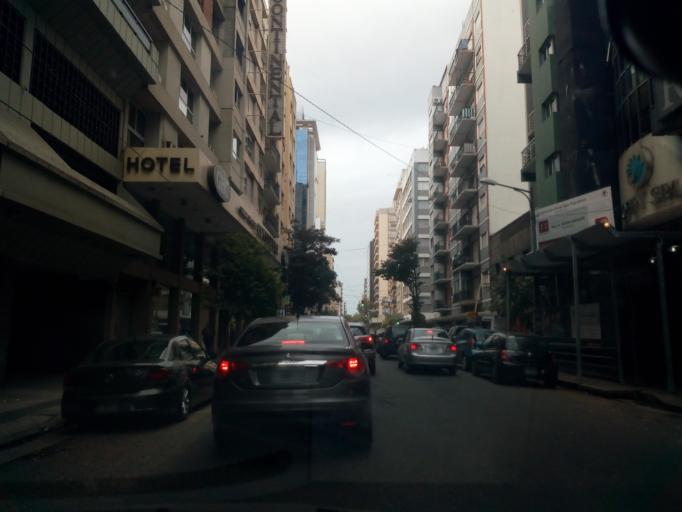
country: AR
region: Buenos Aires
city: Mar del Plata
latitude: -38.0015
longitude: -57.5486
